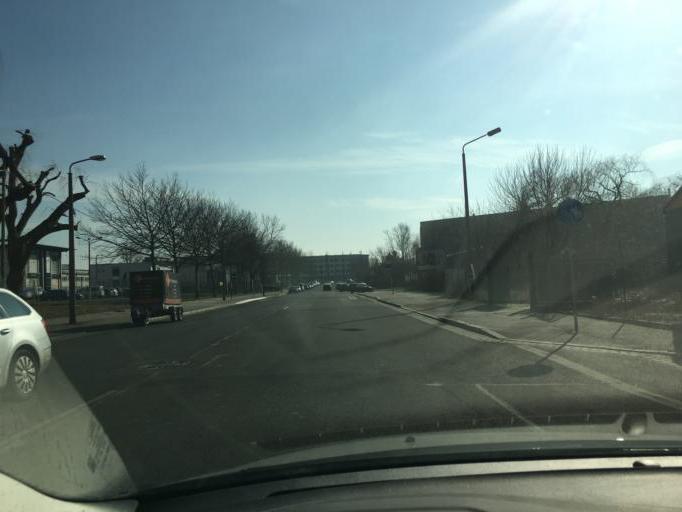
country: DE
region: Saxony
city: Taucha
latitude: 51.3577
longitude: 12.4309
